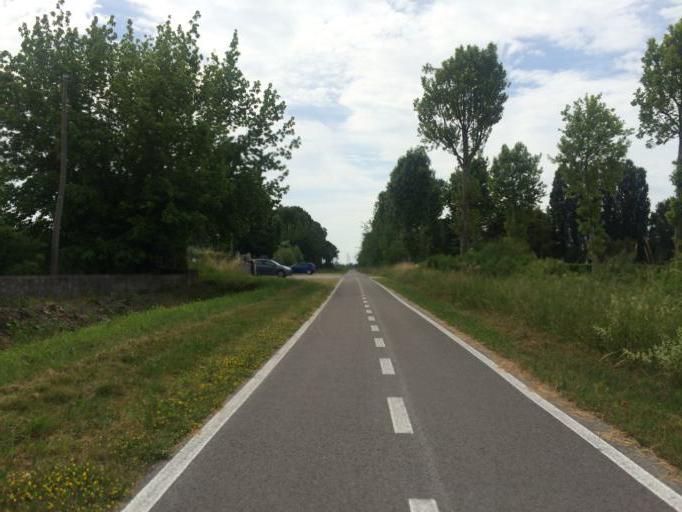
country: IT
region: Friuli Venezia Giulia
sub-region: Provincia di Udine
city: Aquileia
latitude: 45.7460
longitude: 13.3815
